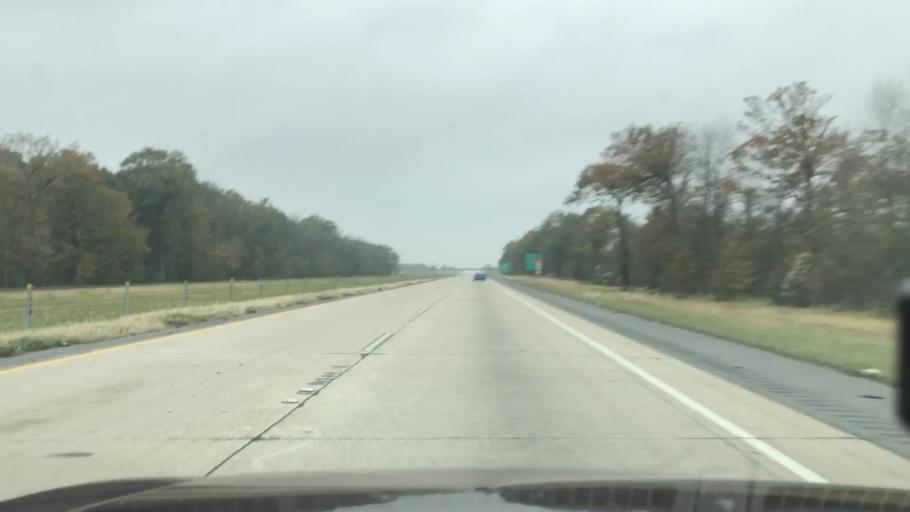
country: US
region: Louisiana
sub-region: Ouachita Parish
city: Lakeshore
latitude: 32.4883
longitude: -91.9811
